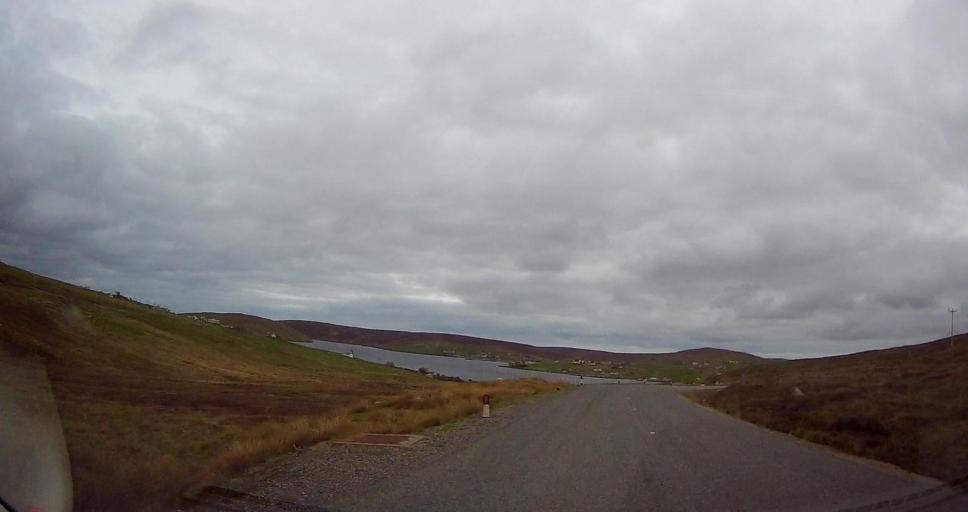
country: GB
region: Scotland
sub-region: Shetland Islands
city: Shetland
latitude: 60.6171
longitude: -1.0749
